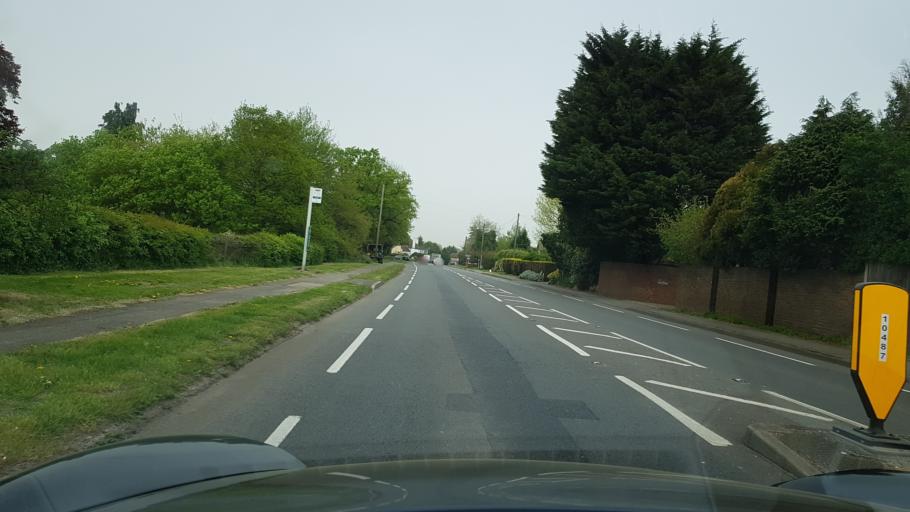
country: GB
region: England
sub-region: Surrey
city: Ripley
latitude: 51.2908
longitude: -0.5022
